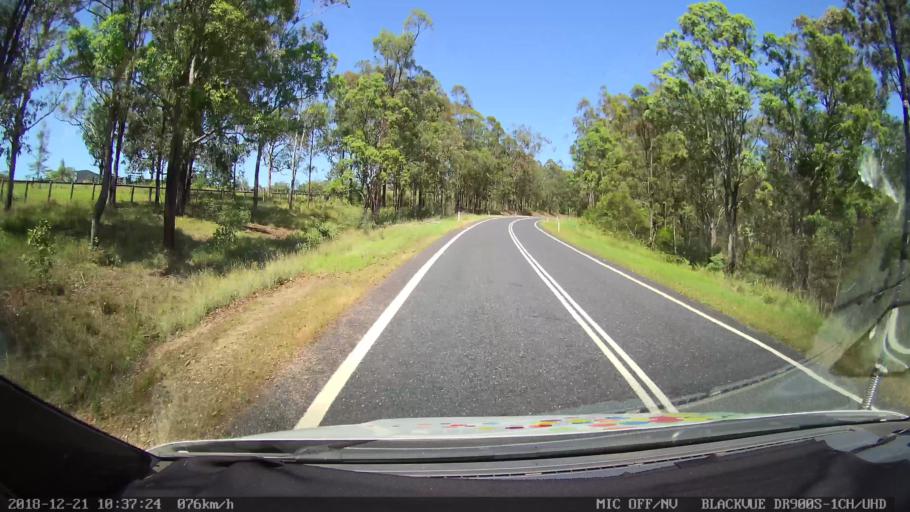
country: AU
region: New South Wales
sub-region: Clarence Valley
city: South Grafton
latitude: -29.6225
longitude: 152.6192
